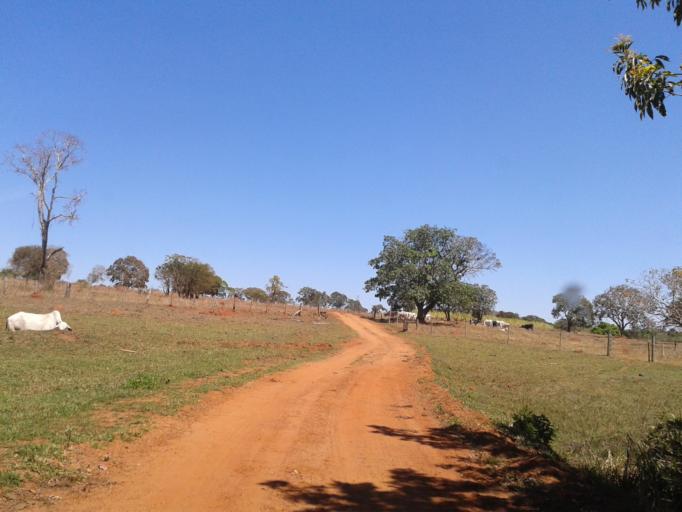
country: BR
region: Minas Gerais
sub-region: Ituiutaba
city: Ituiutaba
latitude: -19.1130
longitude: -49.2769
